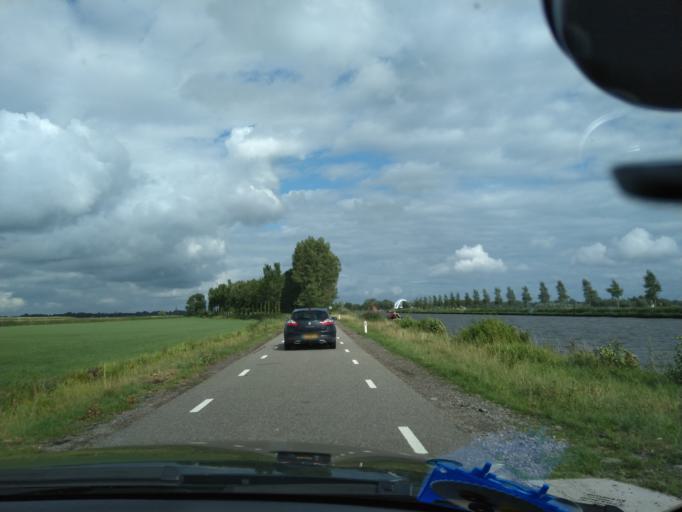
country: NL
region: Groningen
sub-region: Gemeente Zuidhorn
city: Noordhorn
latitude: 53.2544
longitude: 6.3637
